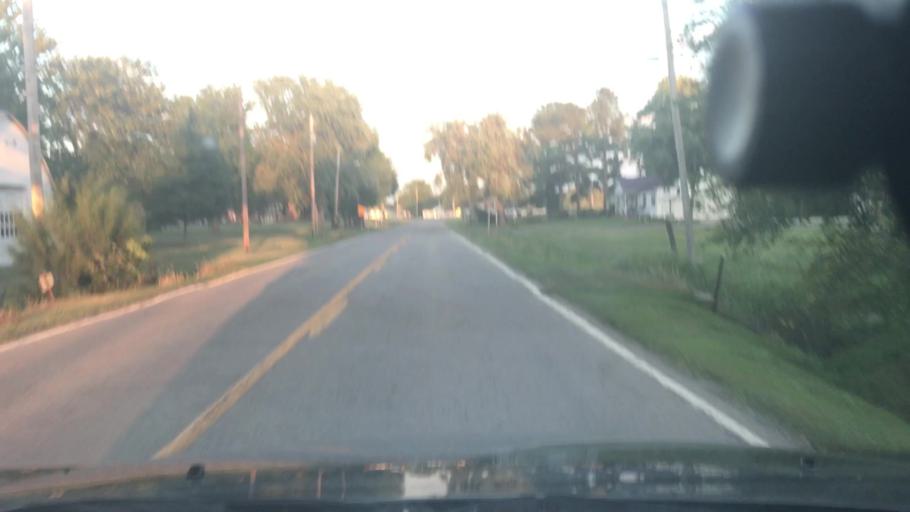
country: US
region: Illinois
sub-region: Washington County
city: Okawville
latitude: 38.3917
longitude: -89.4911
